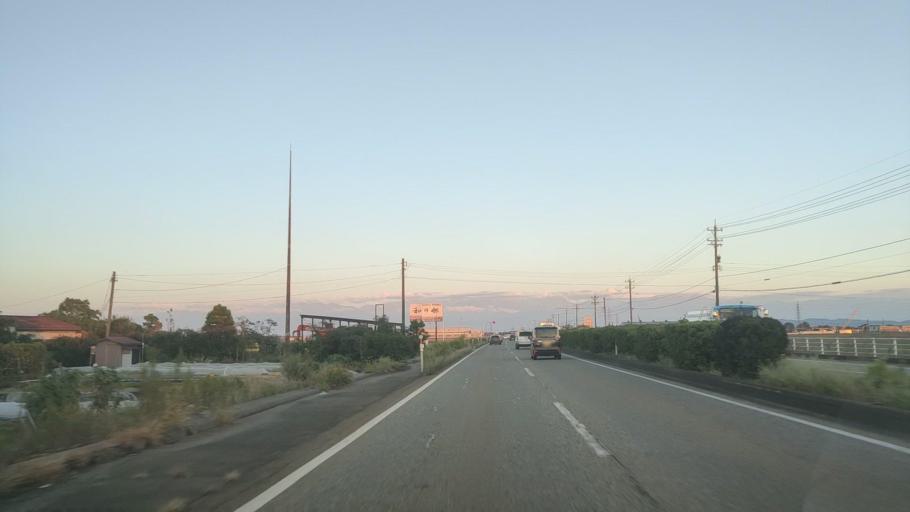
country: JP
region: Toyama
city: Nishishinminato
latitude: 36.7489
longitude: 137.0928
